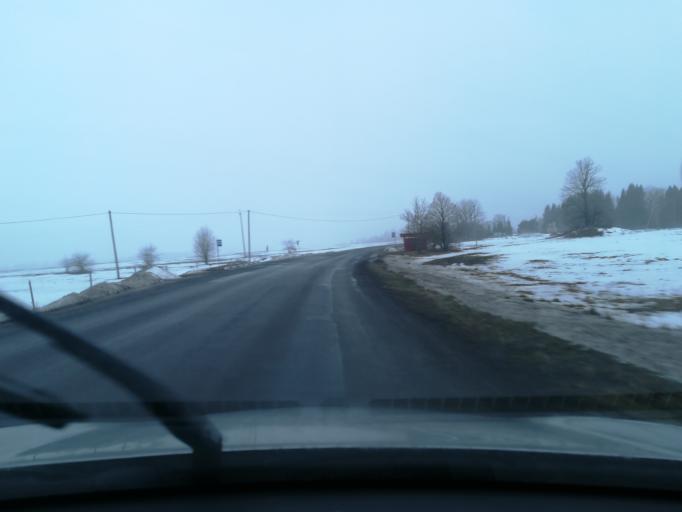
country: EE
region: Harju
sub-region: Raasiku vald
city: Arukula
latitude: 59.3439
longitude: 25.1125
